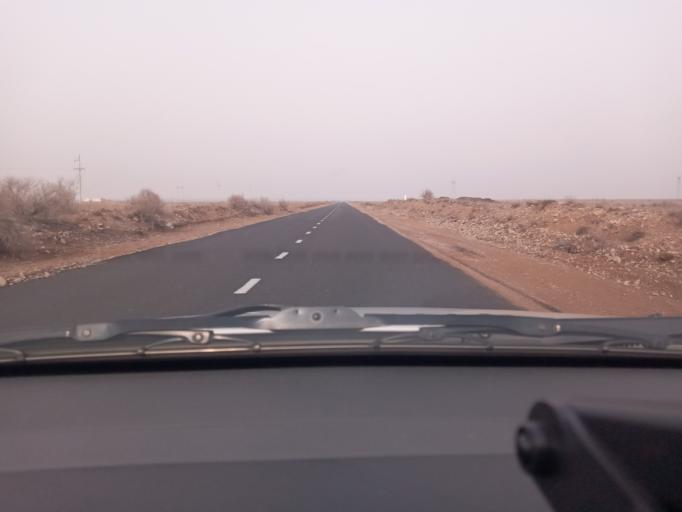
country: UZ
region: Namangan
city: Pop Shahri
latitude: 40.9761
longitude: 70.9707
